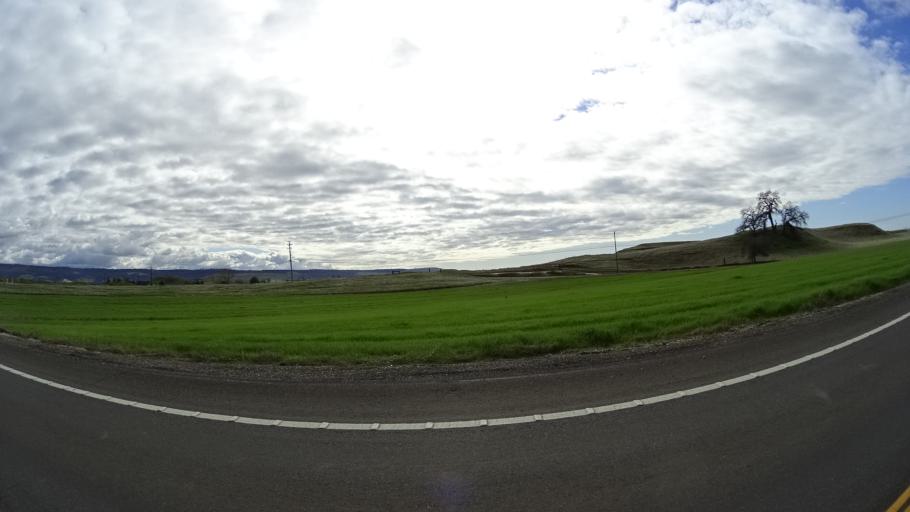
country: US
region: California
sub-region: Butte County
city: Paradise
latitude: 39.6423
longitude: -121.6425
